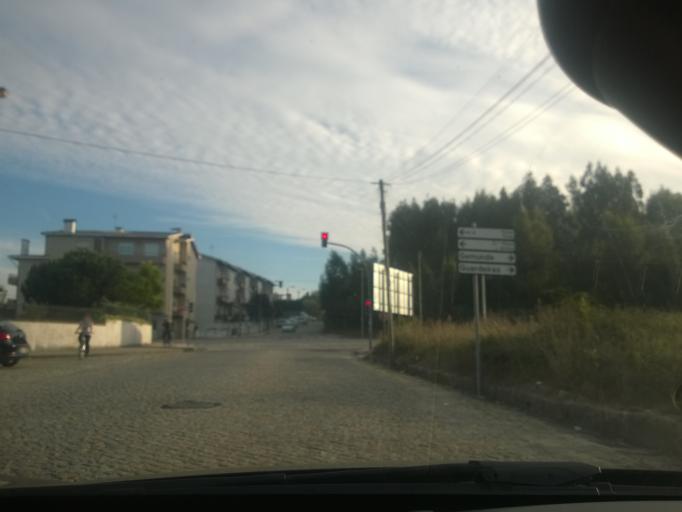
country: PT
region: Porto
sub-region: Maia
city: Anta
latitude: 41.2681
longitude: -8.6189
